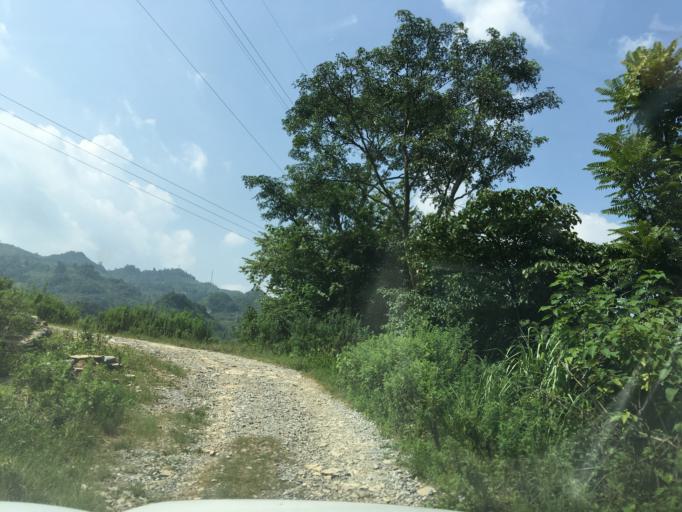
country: CN
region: Guangxi Zhuangzu Zizhiqu
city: Xinzhou
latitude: 24.9908
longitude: 105.7402
